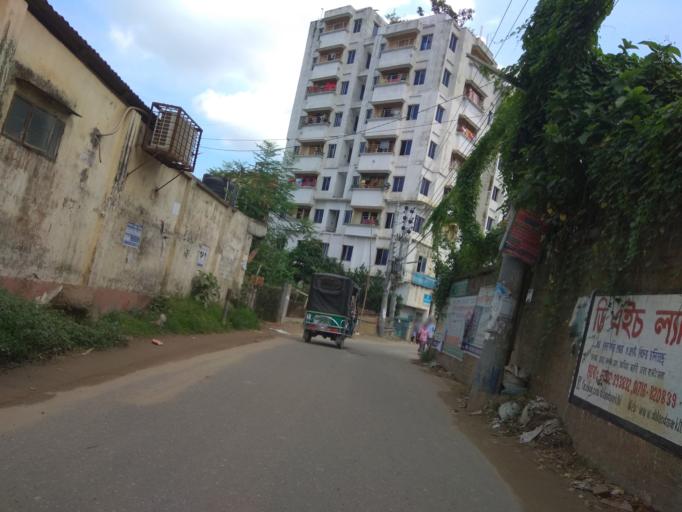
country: BD
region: Dhaka
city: Tungi
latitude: 23.8319
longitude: 90.3891
